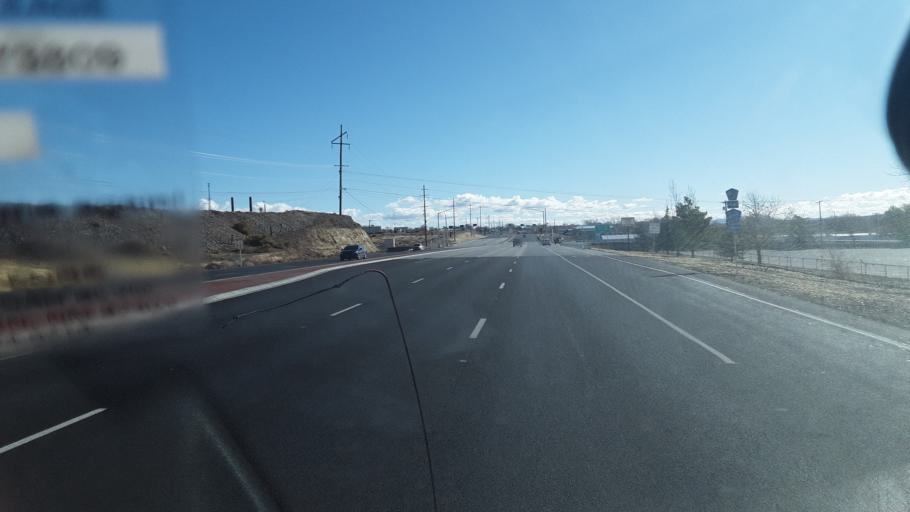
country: US
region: New Mexico
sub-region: San Juan County
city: Lee Acres
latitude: 36.7026
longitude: -108.0975
